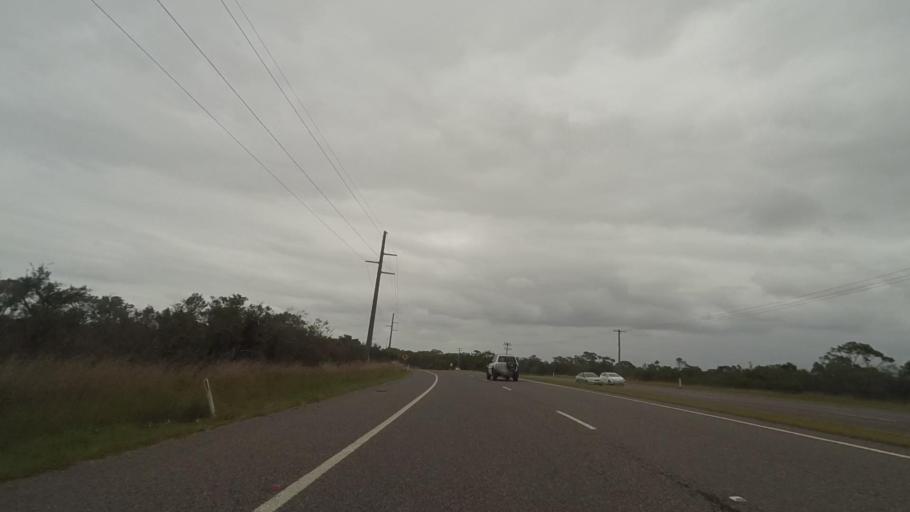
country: AU
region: New South Wales
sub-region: Wyong Shire
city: Kingfisher Shores
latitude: -33.1857
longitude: 151.5863
